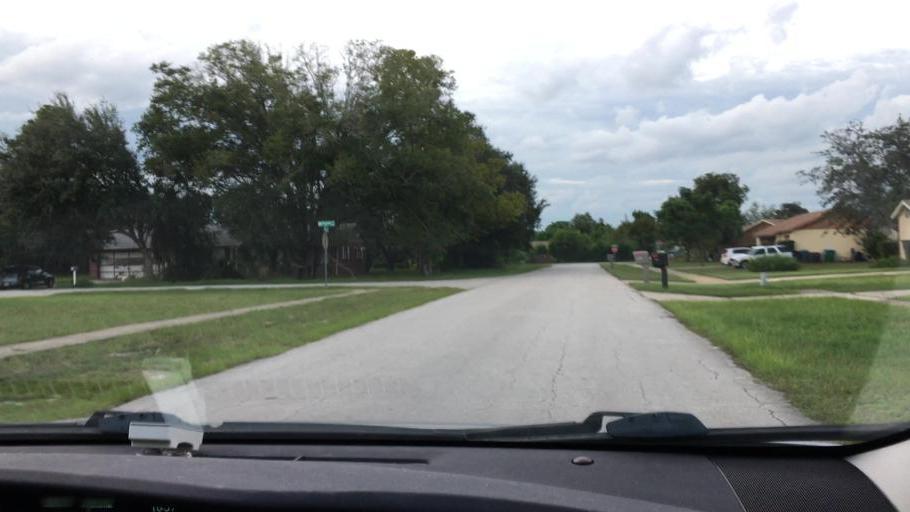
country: US
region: Florida
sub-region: Volusia County
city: Deltona
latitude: 28.8751
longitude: -81.2407
